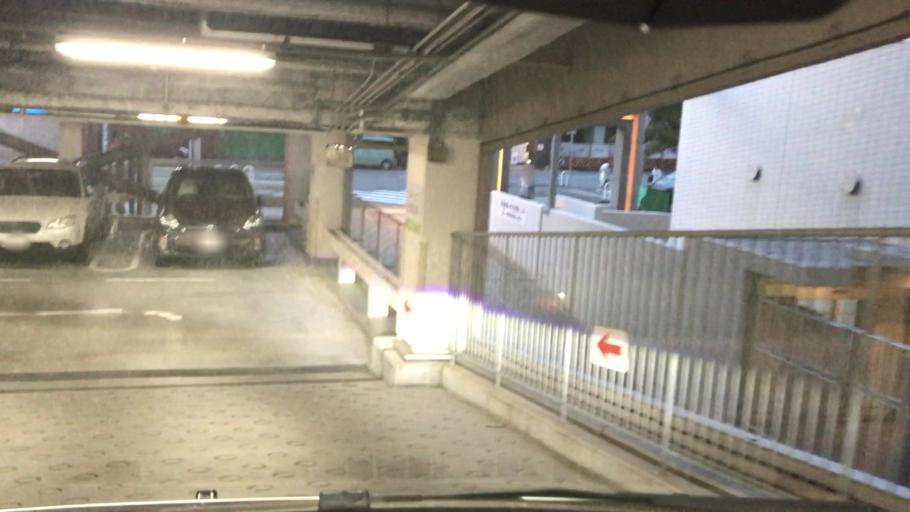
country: JP
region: Hyogo
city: Kobe
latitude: 34.6969
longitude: 135.1977
